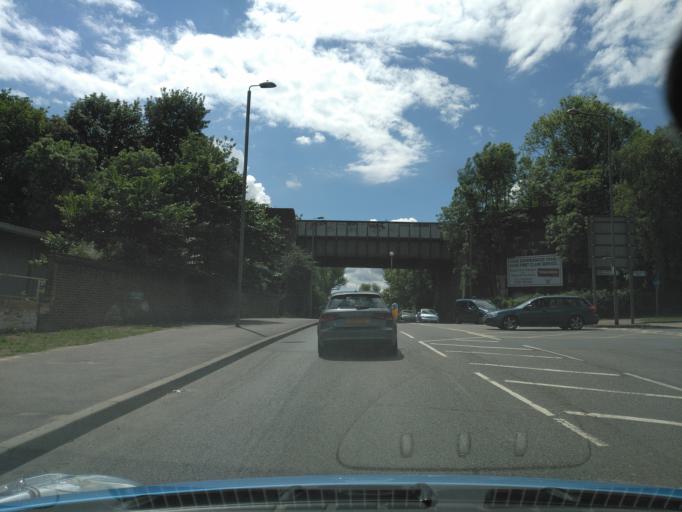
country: GB
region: England
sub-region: Greater London
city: Orpington
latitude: 51.3954
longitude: 0.1121
